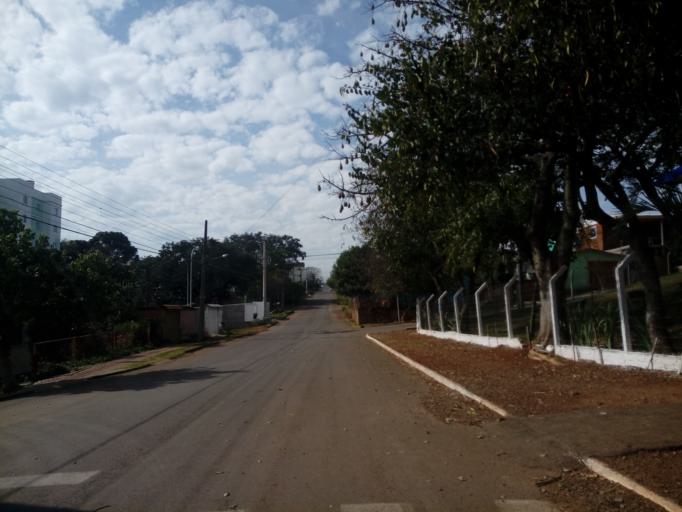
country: BR
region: Santa Catarina
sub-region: Chapeco
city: Chapeco
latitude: -27.1188
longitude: -52.6277
